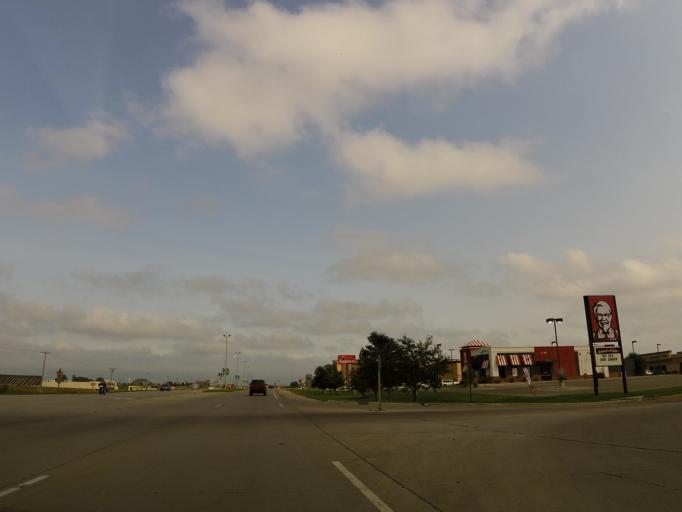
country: US
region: South Dakota
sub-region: Codington County
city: Watertown
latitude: 44.8900
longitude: -97.0739
